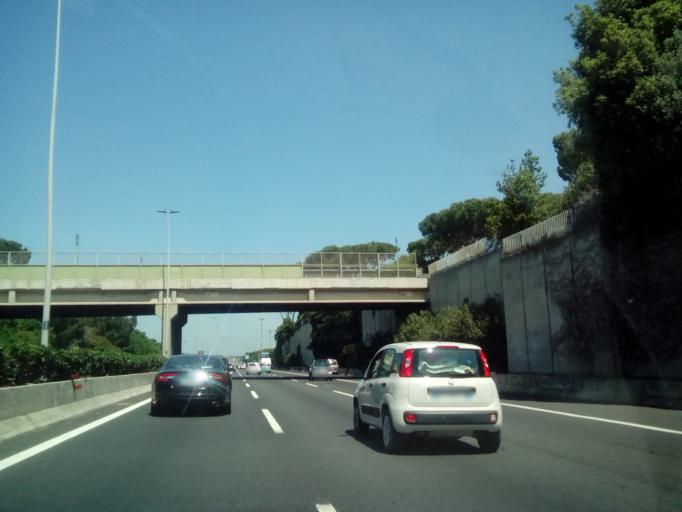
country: IT
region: Latium
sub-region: Citta metropolitana di Roma Capitale
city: Setteville
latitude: 41.9296
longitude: 12.6043
